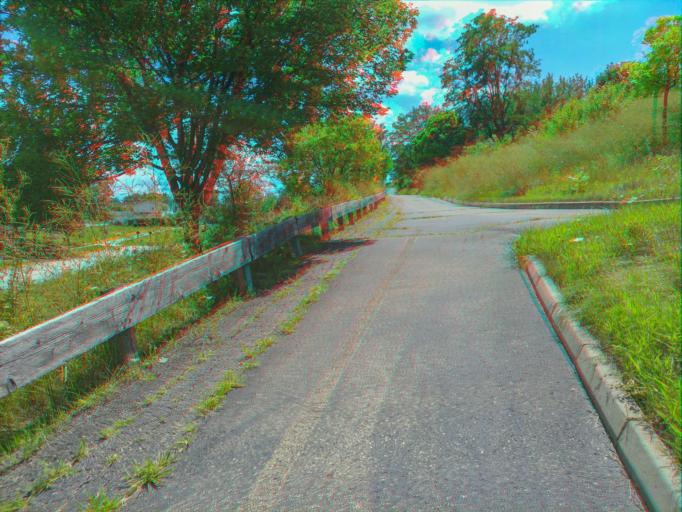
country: US
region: Illinois
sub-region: Lake County
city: Long Grove
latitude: 42.1472
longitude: -87.9951
